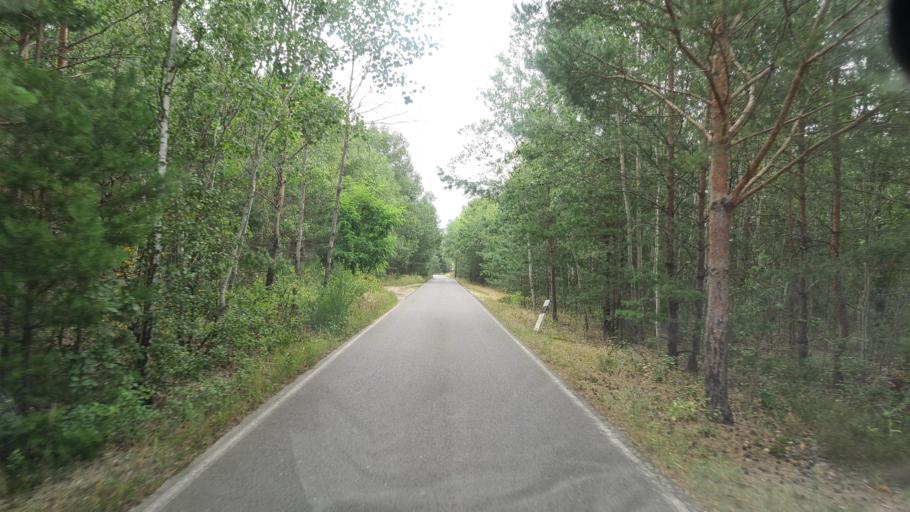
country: DE
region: Brandenburg
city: Finsterwalde
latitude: 51.5833
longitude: 13.7626
